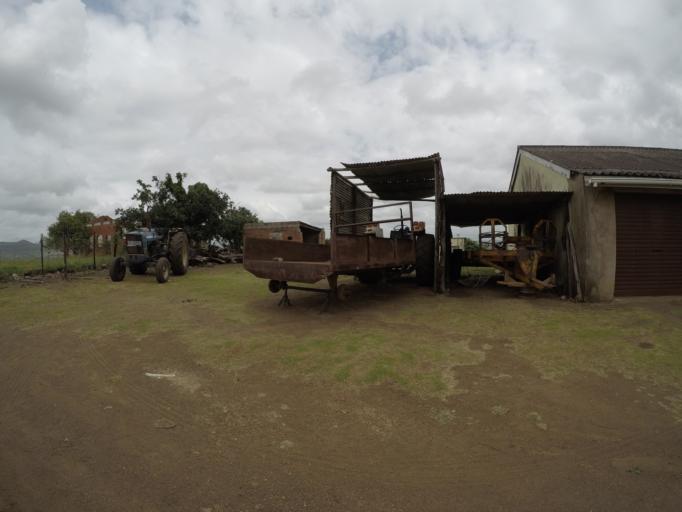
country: ZA
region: KwaZulu-Natal
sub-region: uThungulu District Municipality
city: Empangeni
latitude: -28.6081
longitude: 31.8925
